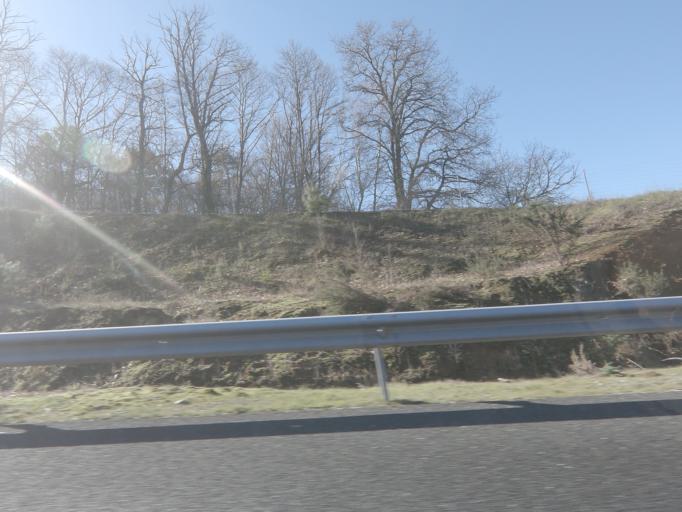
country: ES
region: Galicia
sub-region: Provincia de Pontevedra
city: Lalin
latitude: 42.6259
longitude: -8.1155
